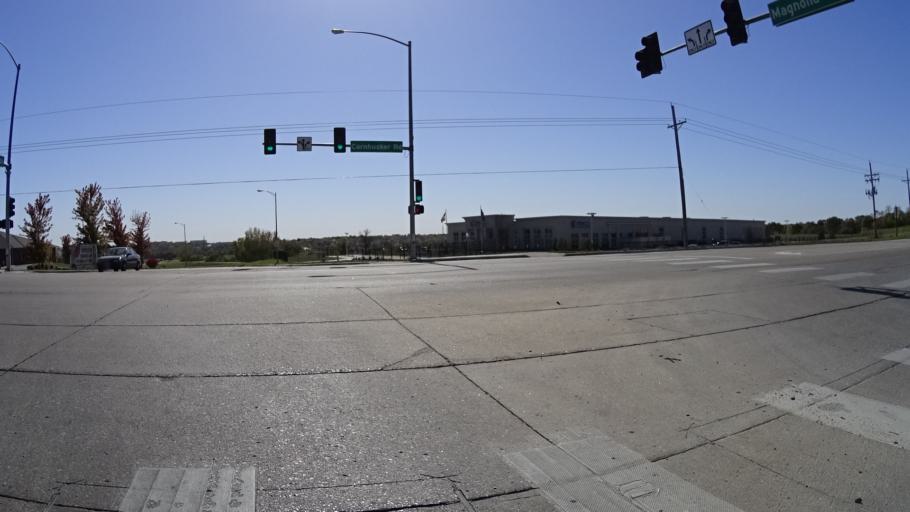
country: US
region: Nebraska
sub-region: Sarpy County
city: Papillion
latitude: 41.1619
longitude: -96.0278
